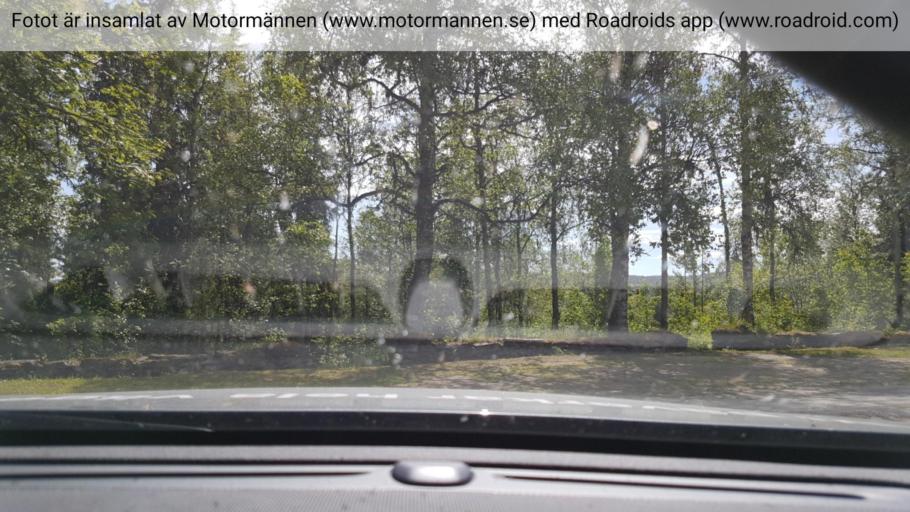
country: SE
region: Vaesterbotten
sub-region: Vilhelmina Kommun
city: Sjoberg
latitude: 65.2369
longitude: 15.9910
